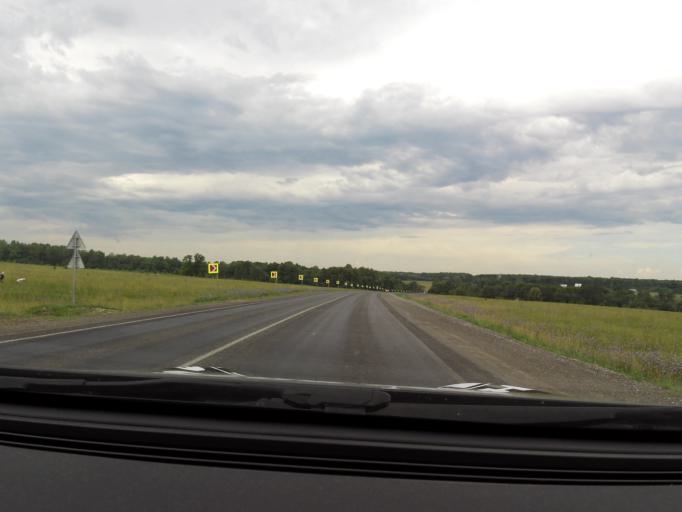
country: RU
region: Bashkortostan
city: Urman
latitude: 54.8185
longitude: 56.8737
